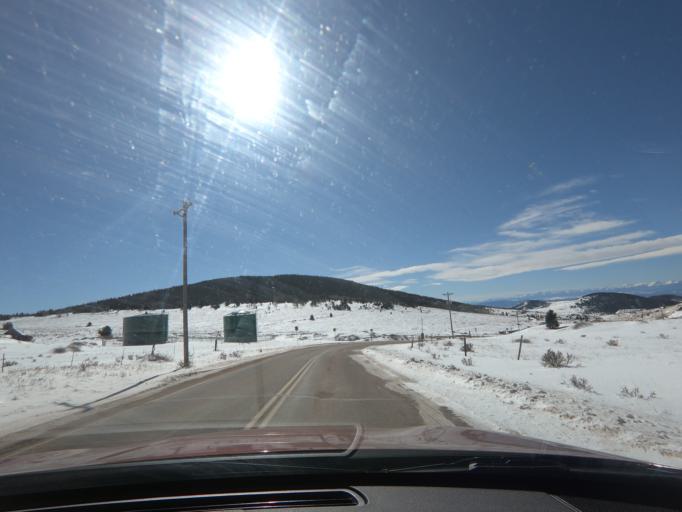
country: US
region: Colorado
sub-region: Teller County
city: Cripple Creek
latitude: 38.7293
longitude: -105.1194
